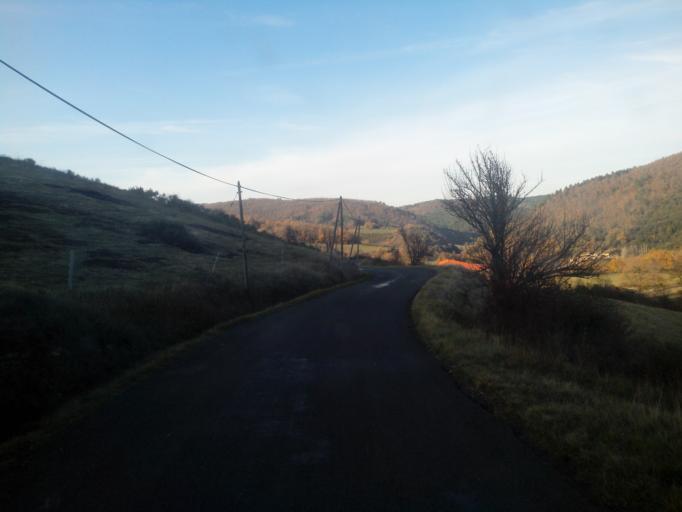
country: FR
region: Languedoc-Roussillon
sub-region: Departement de l'Aude
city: Couiza
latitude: 42.8834
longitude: 2.3206
